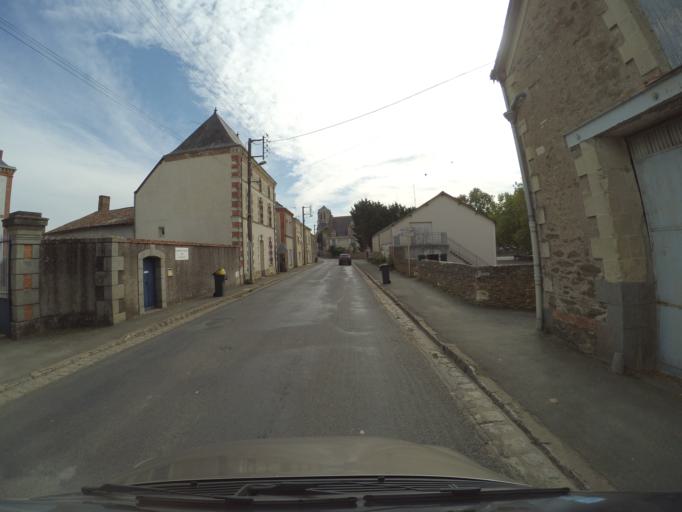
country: FR
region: Pays de la Loire
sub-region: Departement de Maine-et-Loire
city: Vihiers
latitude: 47.2140
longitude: -0.5962
